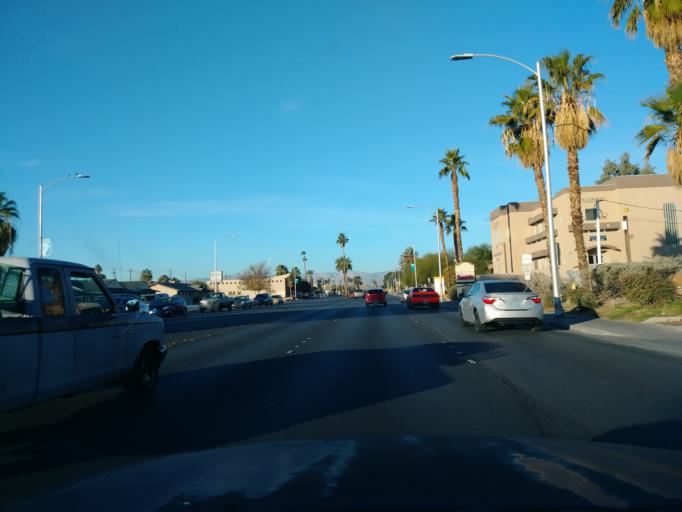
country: US
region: Nevada
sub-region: Clark County
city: Las Vegas
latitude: 36.1590
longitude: -115.1741
